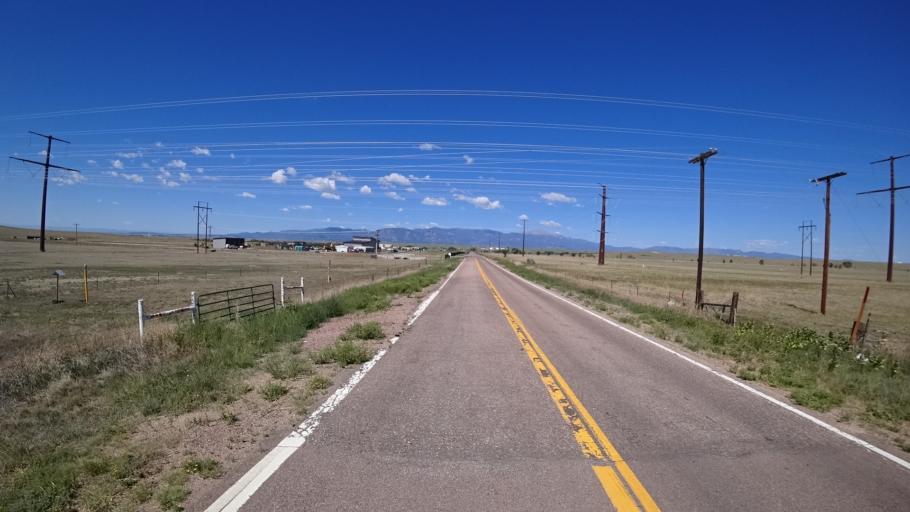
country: US
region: Colorado
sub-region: El Paso County
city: Security-Widefield
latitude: 38.7810
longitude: -104.6271
